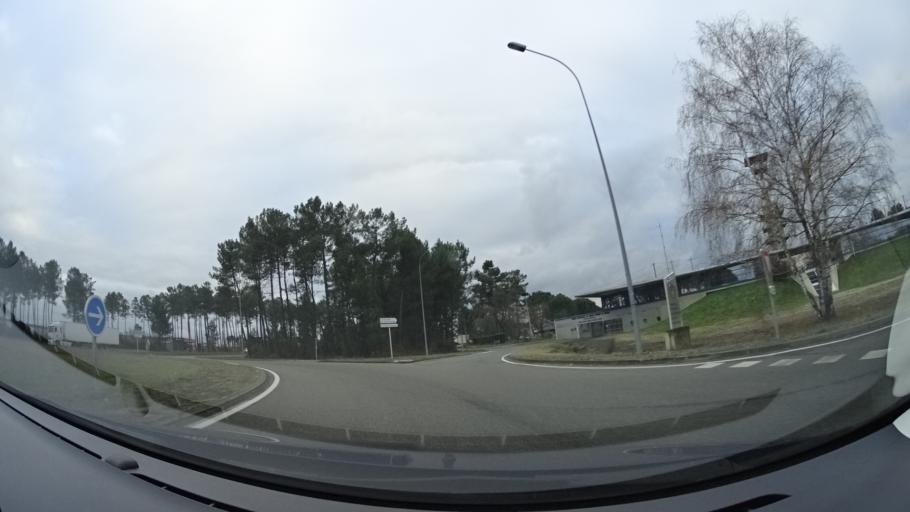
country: FR
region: Aquitaine
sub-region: Departement des Landes
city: Mont-de-Marsan
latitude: 43.9172
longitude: -0.4520
